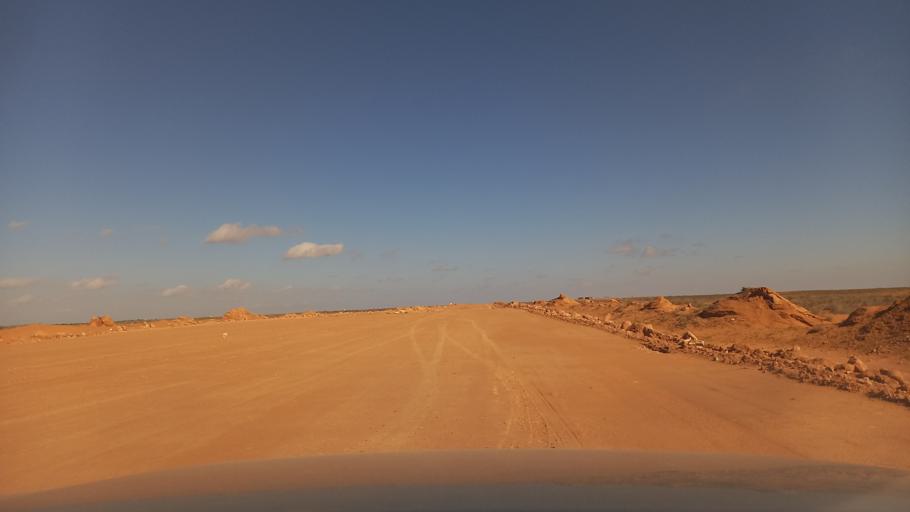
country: TN
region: Madanin
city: Medenine
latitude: 33.2402
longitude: 10.5554
